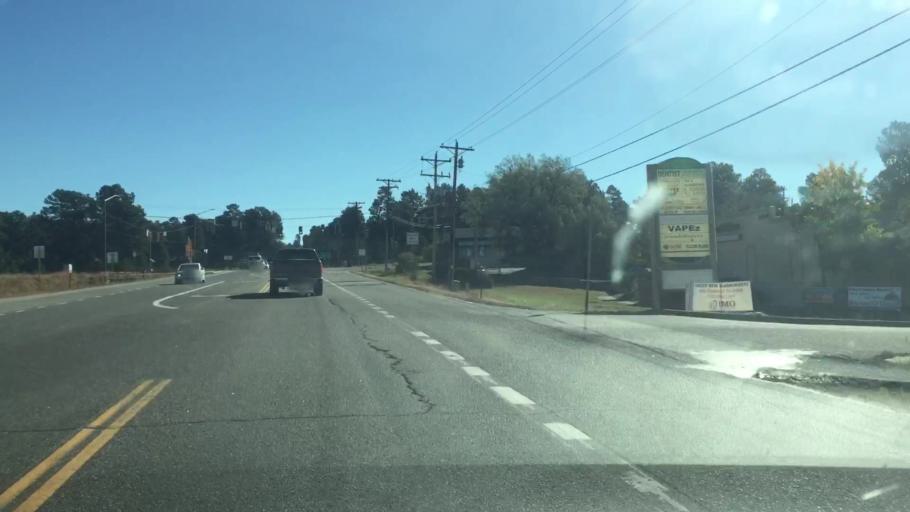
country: US
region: Colorado
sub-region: Elbert County
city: Elizabeth
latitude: 39.3615
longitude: -104.5911
